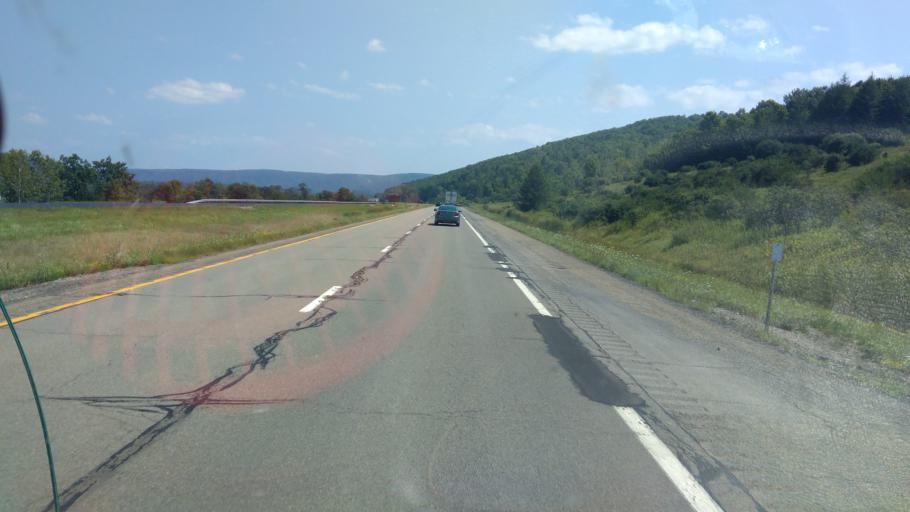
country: US
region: New York
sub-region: Allegany County
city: Alfred
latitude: 42.3171
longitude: -77.7947
